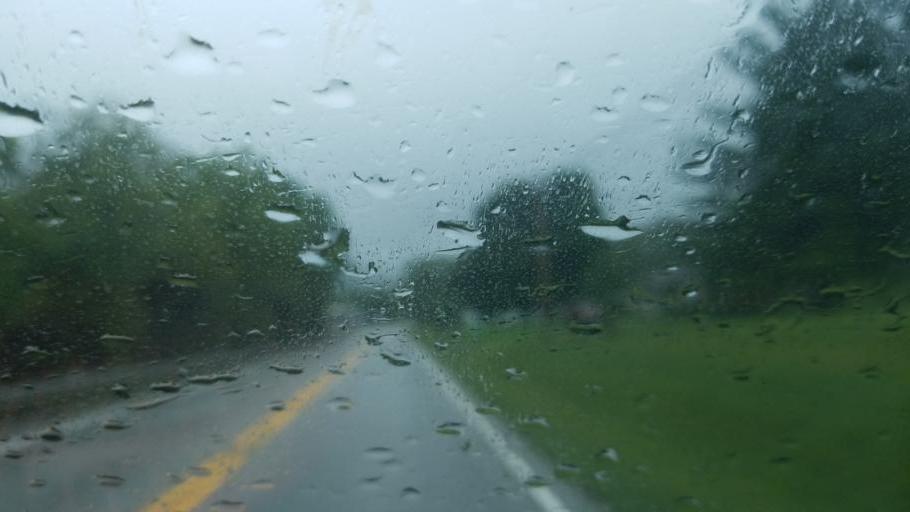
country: US
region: Kentucky
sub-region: Fleming County
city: Flemingsburg
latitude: 38.3683
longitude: -83.6215
